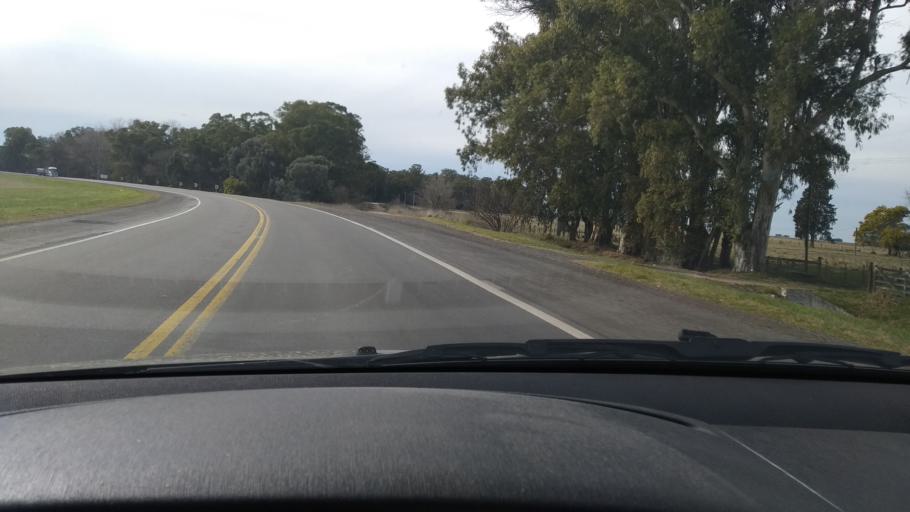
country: AR
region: Buenos Aires
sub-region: Partido de Azul
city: Azul
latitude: -36.7635
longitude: -59.8067
